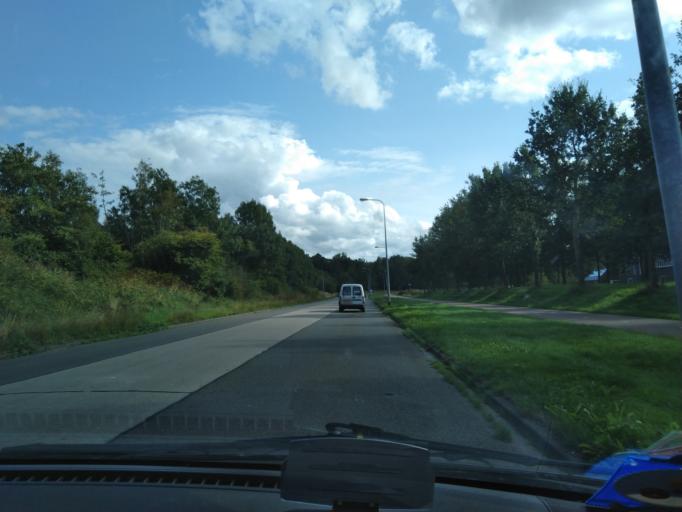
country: NL
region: Groningen
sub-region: Gemeente Groningen
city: Groningen
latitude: 53.1827
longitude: 6.5455
